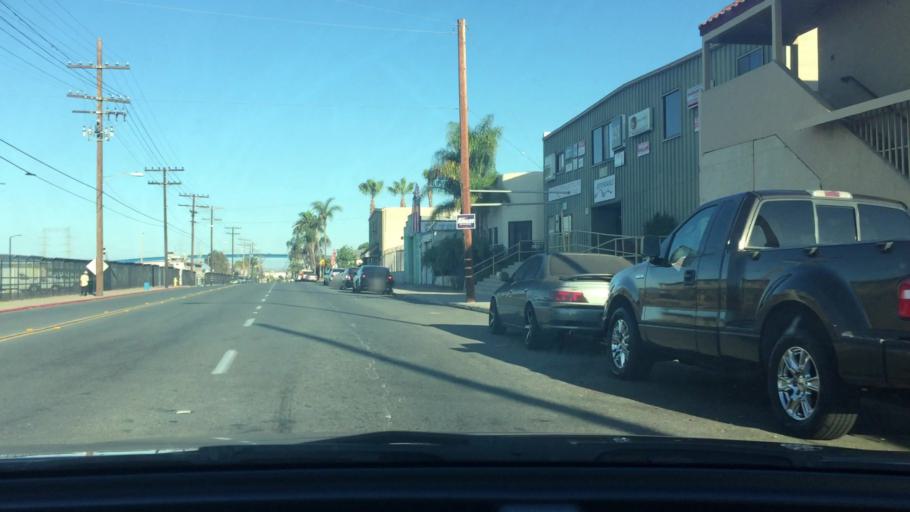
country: US
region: California
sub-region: San Diego County
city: National City
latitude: 32.6929
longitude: -117.1262
